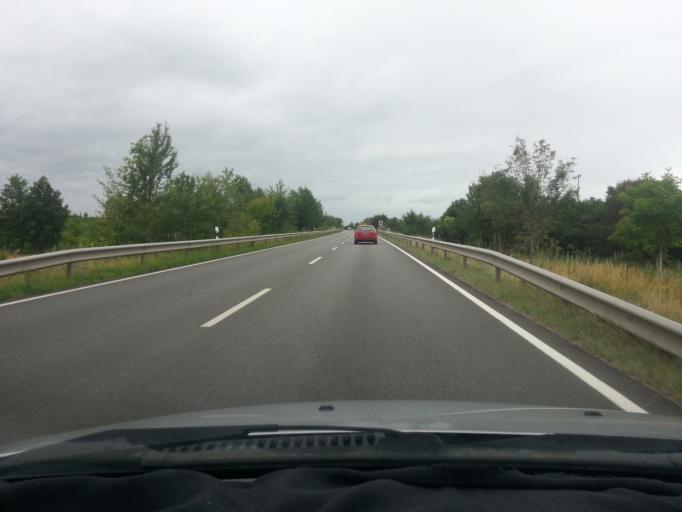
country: DE
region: Rheinland-Pfalz
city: Niederkirchen bei Deidesheim
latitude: 49.4194
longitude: 8.2005
